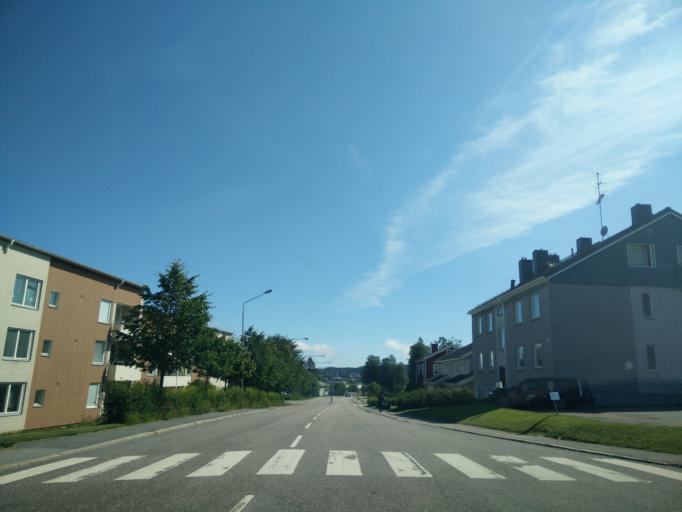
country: SE
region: Vaesternorrland
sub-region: Haernoesands Kommun
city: Haernoesand
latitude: 62.6362
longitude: 17.9180
